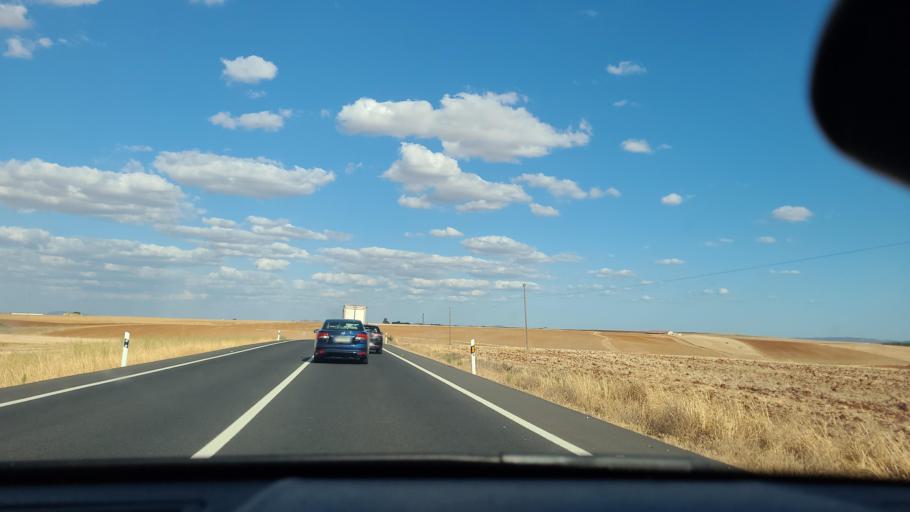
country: ES
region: Extremadura
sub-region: Provincia de Badajoz
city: Berlanga
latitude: 38.2651
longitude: -5.7519
